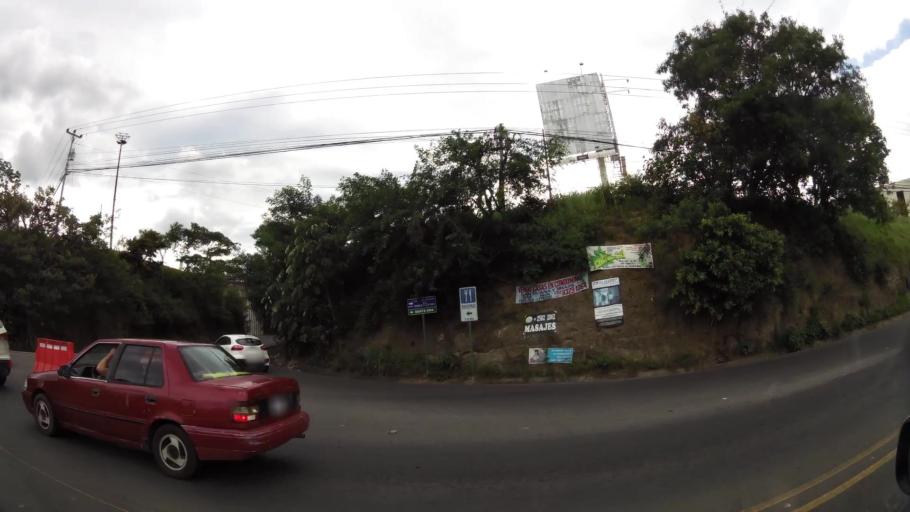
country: CR
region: San Jose
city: Santa Ana
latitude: 9.9451
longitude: -84.1911
